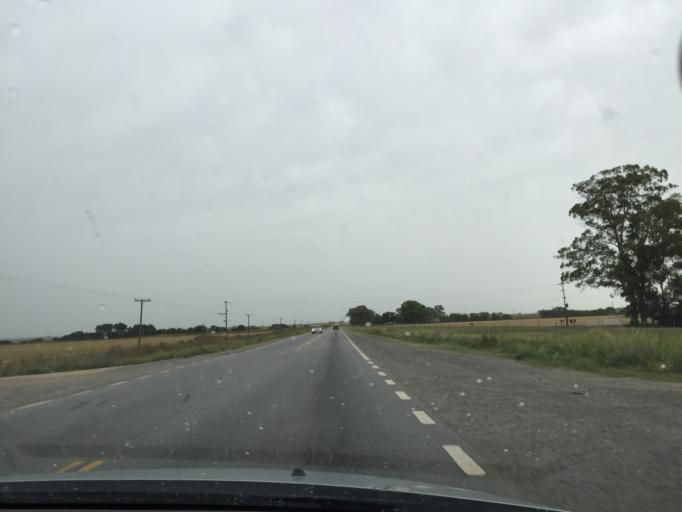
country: AR
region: Buenos Aires
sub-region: Partido de Tandil
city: Tandil
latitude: -37.5617
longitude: -58.7884
